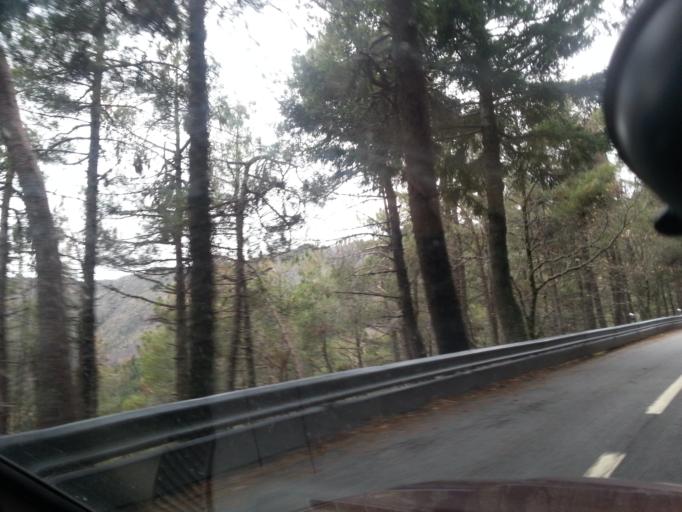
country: PT
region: Guarda
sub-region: Manteigas
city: Manteigas
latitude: 40.4136
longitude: -7.5458
